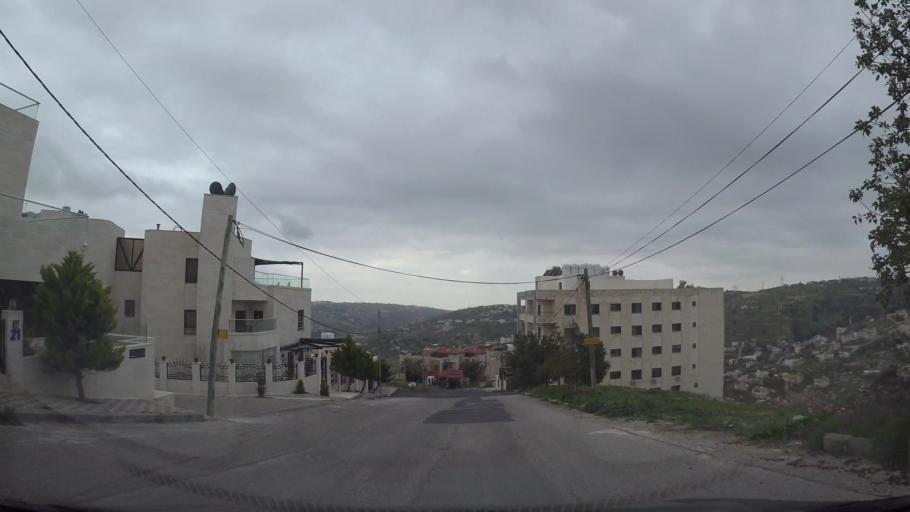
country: JO
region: Amman
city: Wadi as Sir
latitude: 31.9629
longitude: 35.8195
